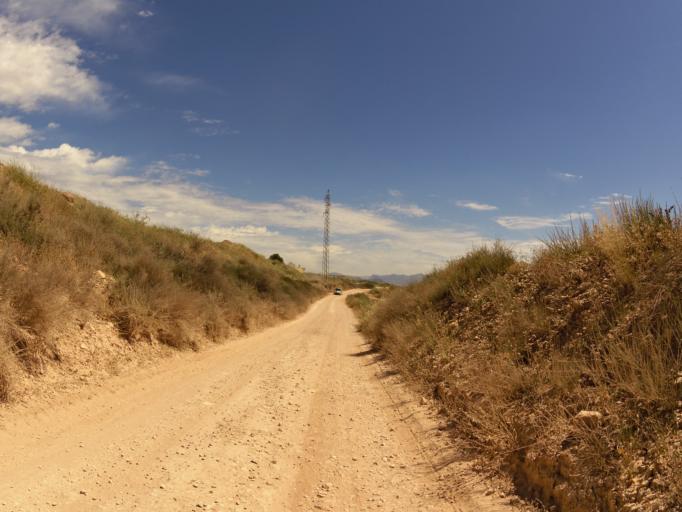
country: ES
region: Valencia
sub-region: Provincia de Alicante
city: Agost
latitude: 38.3994
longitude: -0.6095
